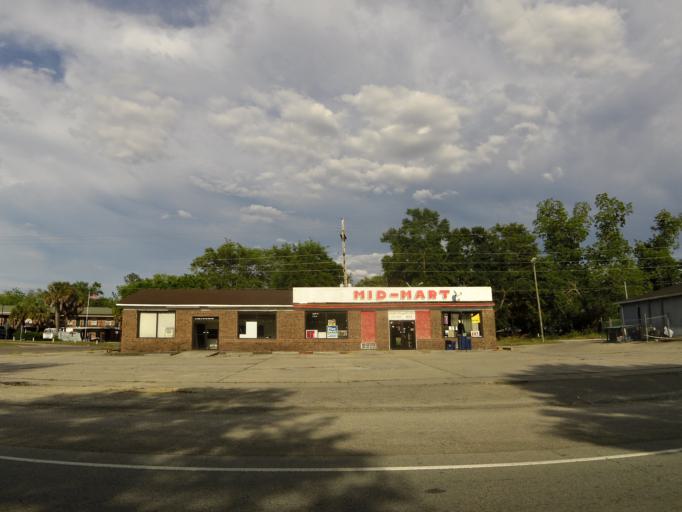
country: US
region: South Carolina
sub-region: Hampton County
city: Estill
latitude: 32.7582
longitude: -81.2412
